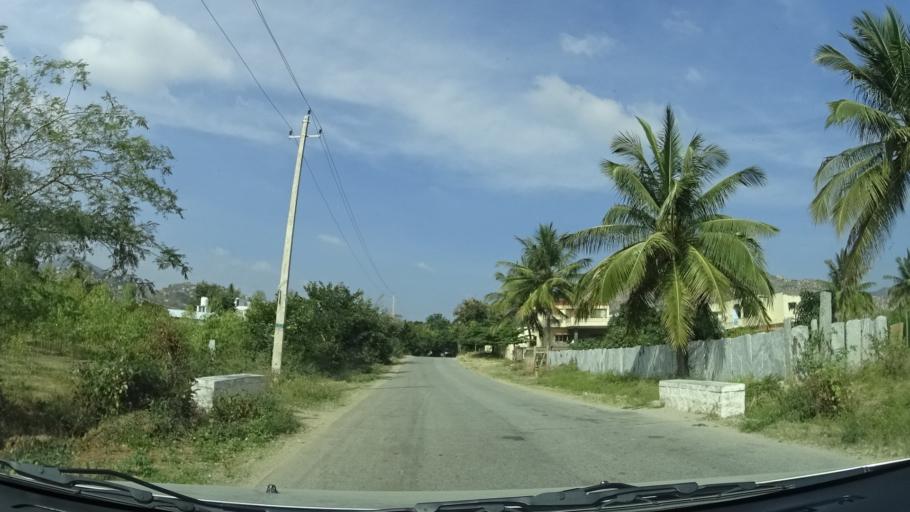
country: IN
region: Karnataka
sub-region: Chikkaballapur
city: Chik Ballapur
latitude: 13.4066
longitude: 77.7018
